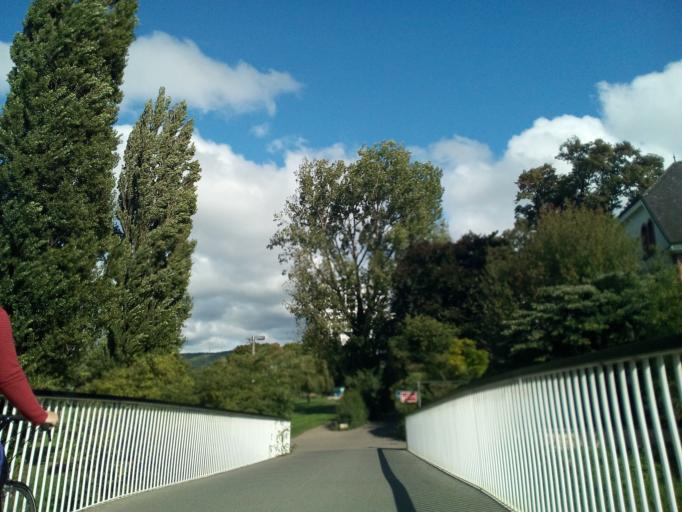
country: CH
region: Basel-Landschaft
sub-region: Bezirk Arlesheim
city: Birsfelden
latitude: 47.5574
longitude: 7.6178
